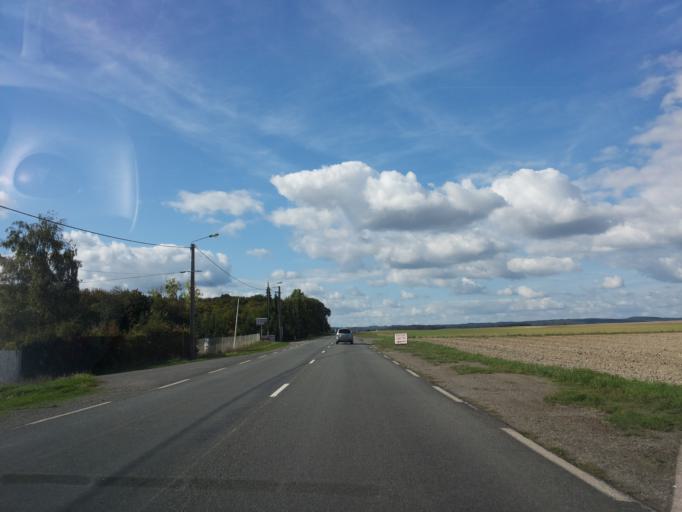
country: FR
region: Champagne-Ardenne
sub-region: Departement de la Marne
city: Cormicy
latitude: 49.4266
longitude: 3.8693
